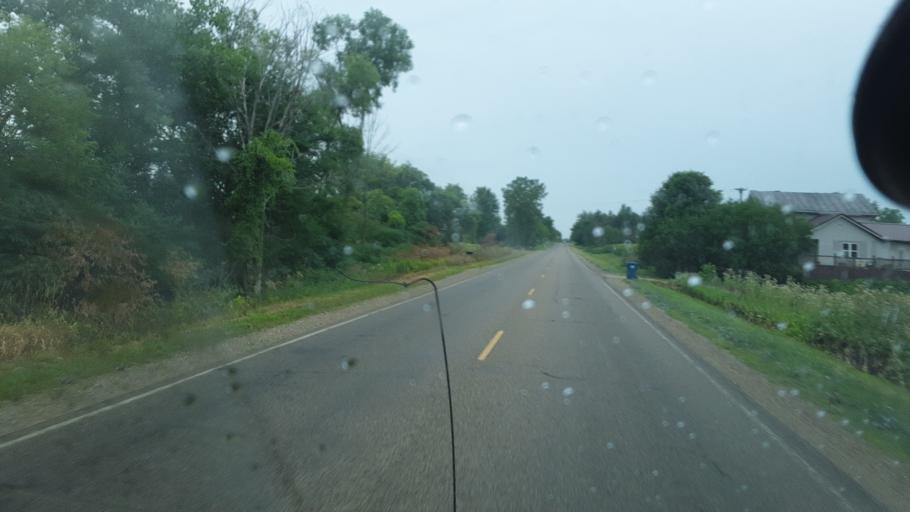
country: US
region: Michigan
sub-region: Hillsdale County
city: Reading
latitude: 41.7077
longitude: -84.7868
